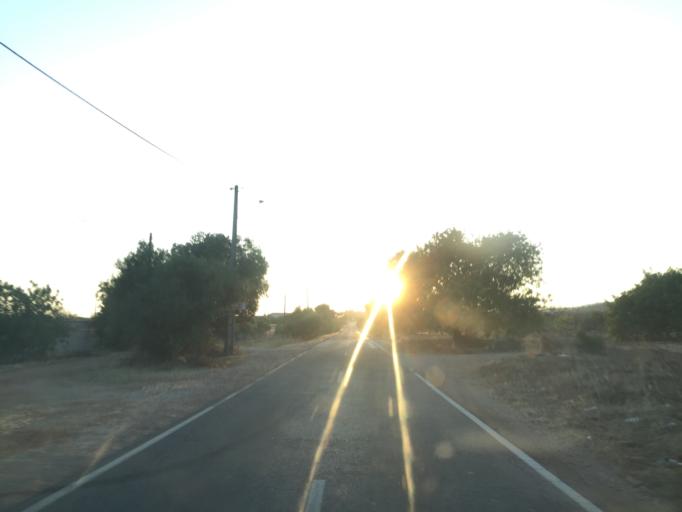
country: PT
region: Faro
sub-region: Faro
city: Santa Barbara de Nexe
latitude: 37.0906
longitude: -7.9309
